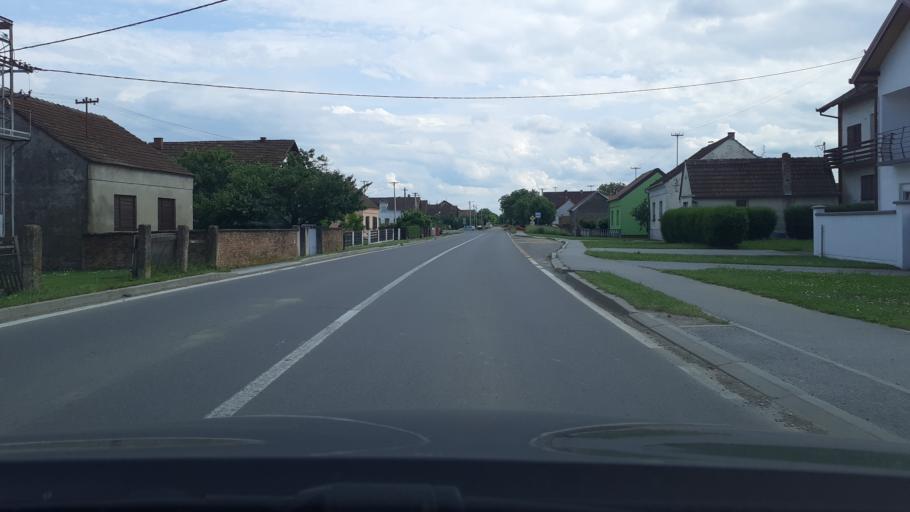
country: HR
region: Brodsko-Posavska
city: Slobodnica
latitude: 45.1741
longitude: 17.9284
